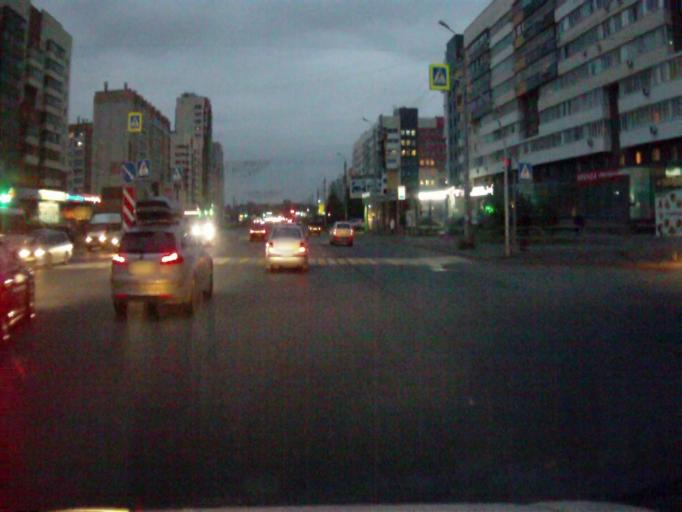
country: RU
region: Chelyabinsk
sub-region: Gorod Chelyabinsk
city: Chelyabinsk
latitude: 55.1671
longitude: 61.2948
